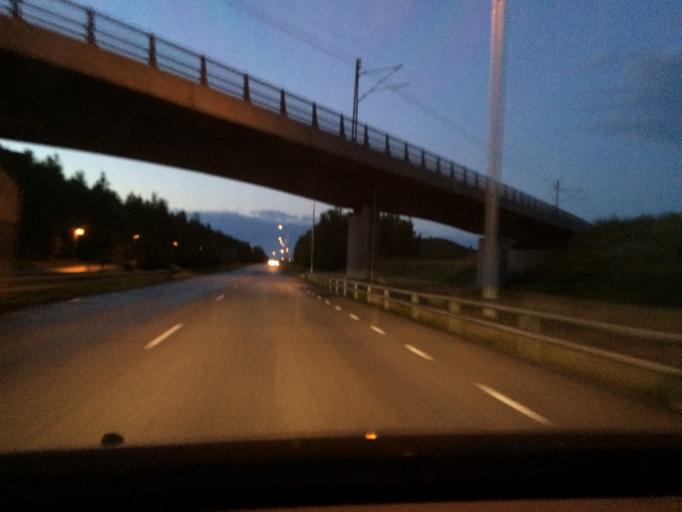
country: SE
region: Skane
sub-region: Malmo
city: Bunkeflostrand
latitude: 55.5586
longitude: 12.9581
